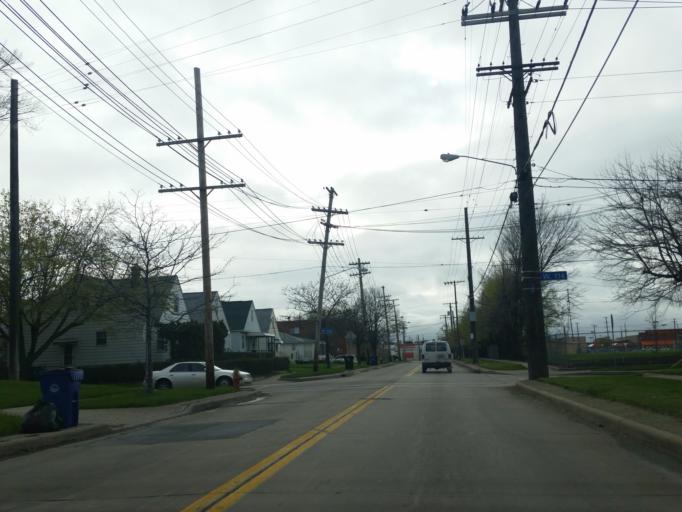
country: US
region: Ohio
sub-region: Cuyahoga County
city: Lakewood
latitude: 41.4704
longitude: -81.7654
